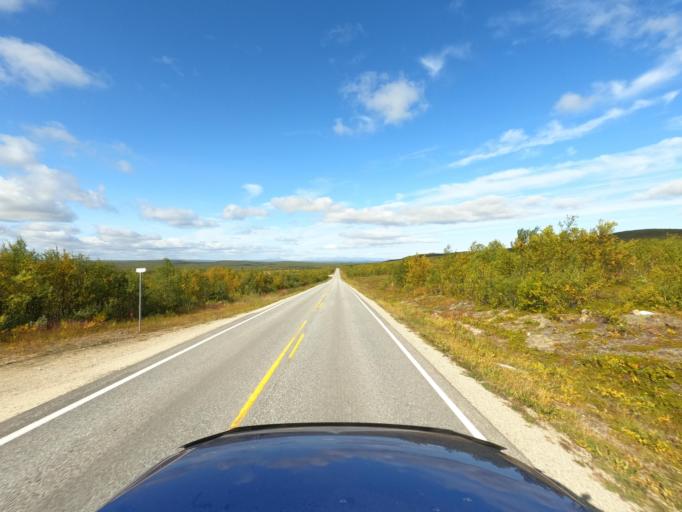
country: NO
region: Finnmark Fylke
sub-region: Karasjok
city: Karasjohka
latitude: 69.5587
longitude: 25.3946
